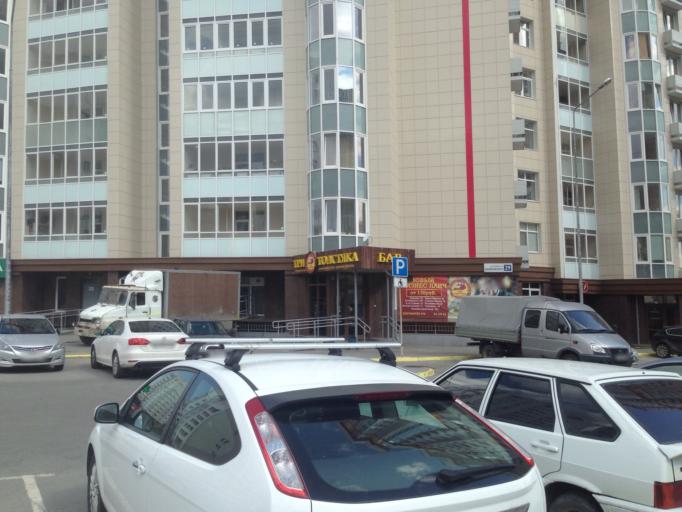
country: RU
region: Sverdlovsk
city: Yekaterinburg
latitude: 56.8047
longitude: 60.6028
